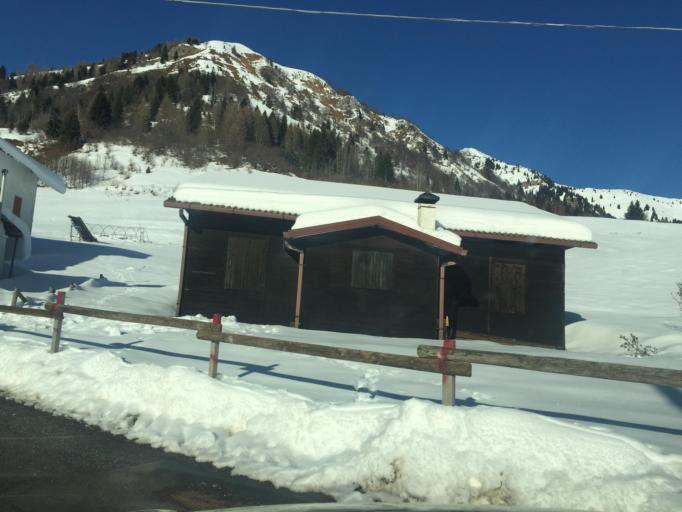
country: IT
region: Friuli Venezia Giulia
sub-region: Provincia di Udine
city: Lauco
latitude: 46.4620
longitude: 12.9347
